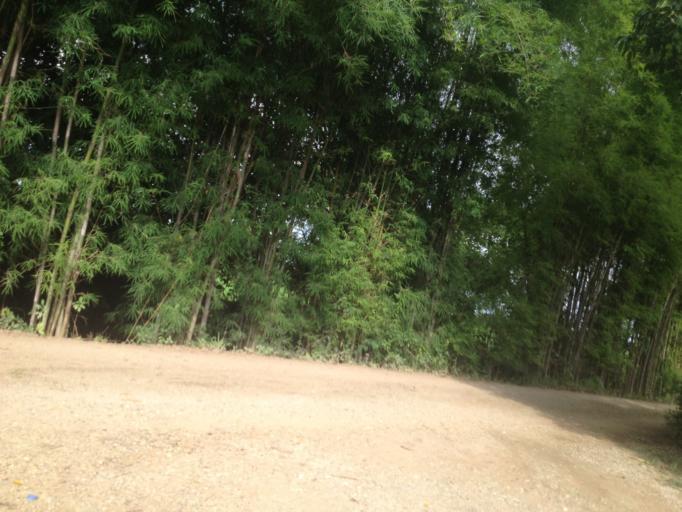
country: TH
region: Chiang Mai
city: Hang Dong
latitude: 18.7050
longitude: 98.9174
